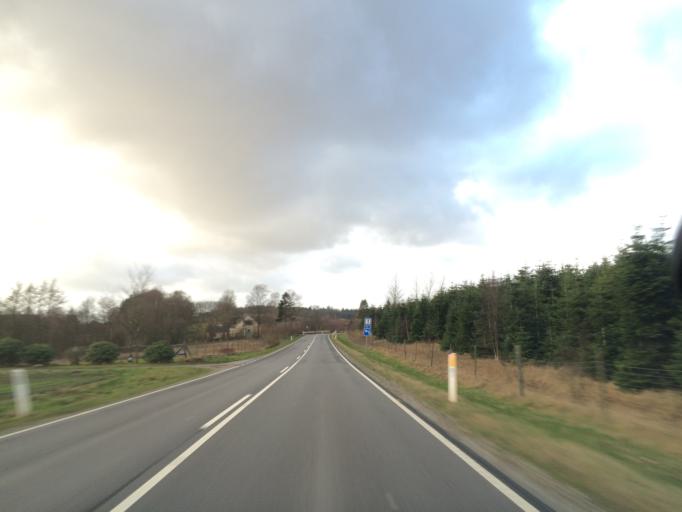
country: DK
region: Central Jutland
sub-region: Silkeborg Kommune
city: Svejbaek
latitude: 56.0926
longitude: 9.6620
